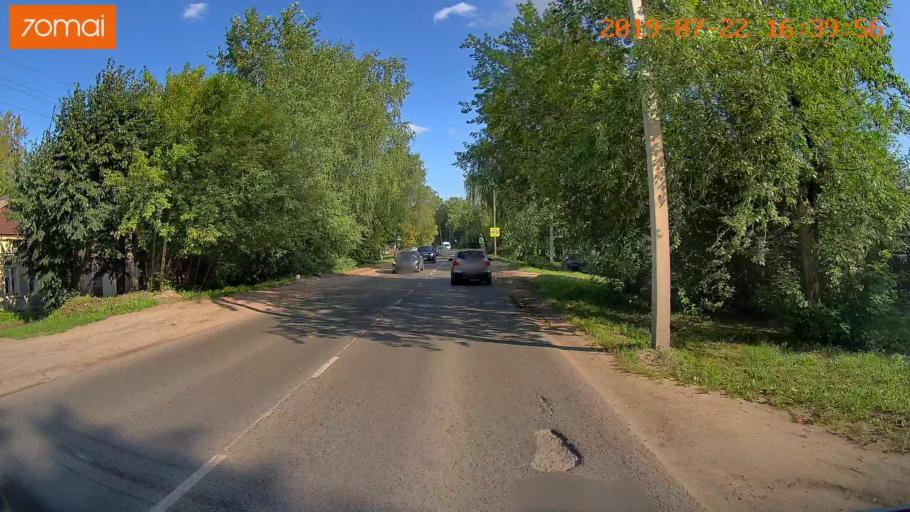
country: RU
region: Ivanovo
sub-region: Gorod Ivanovo
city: Ivanovo
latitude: 57.0250
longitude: 40.9543
